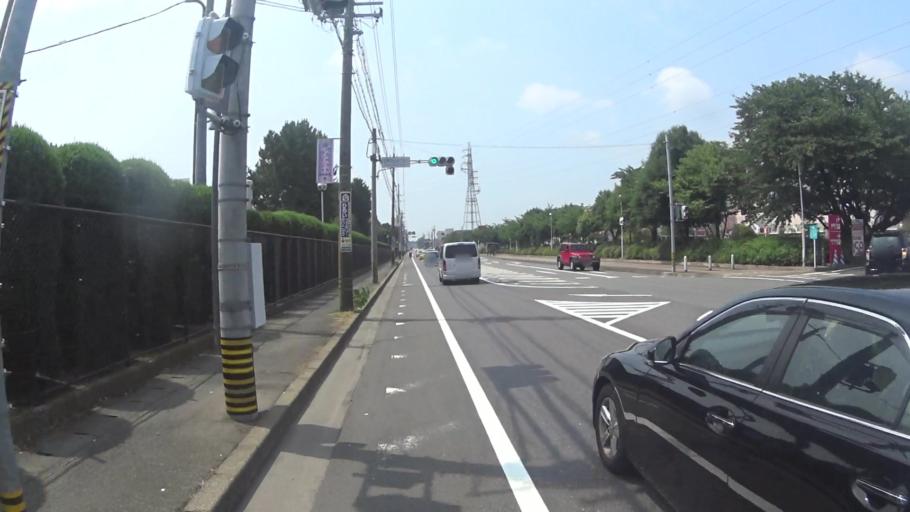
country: JP
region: Mie
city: Suzuka
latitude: 34.8725
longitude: 136.5333
